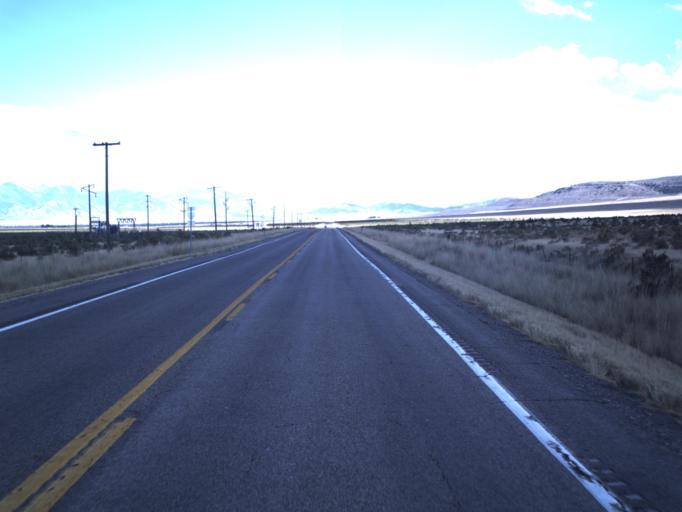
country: US
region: Utah
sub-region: Tooele County
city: Grantsville
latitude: 40.6736
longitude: -112.5490
